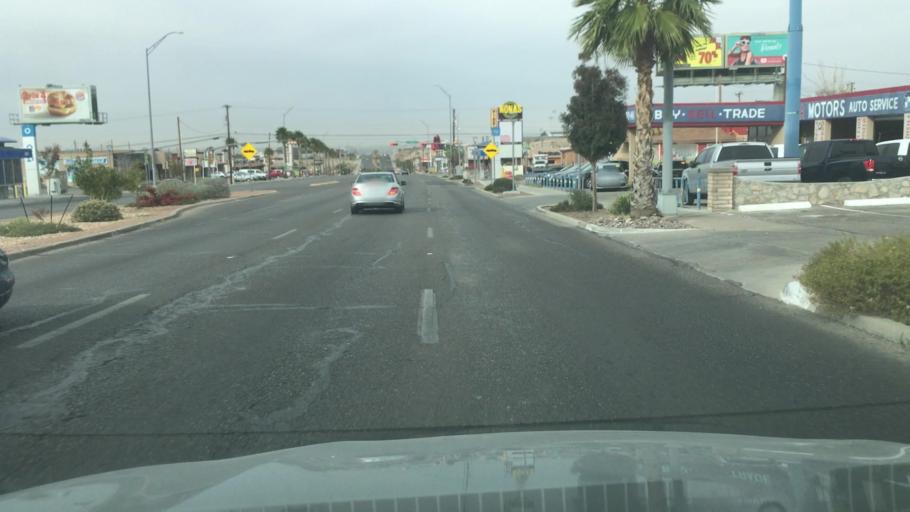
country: US
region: New Mexico
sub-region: Dona Ana County
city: Sunland Park
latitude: 31.8328
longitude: -106.5357
